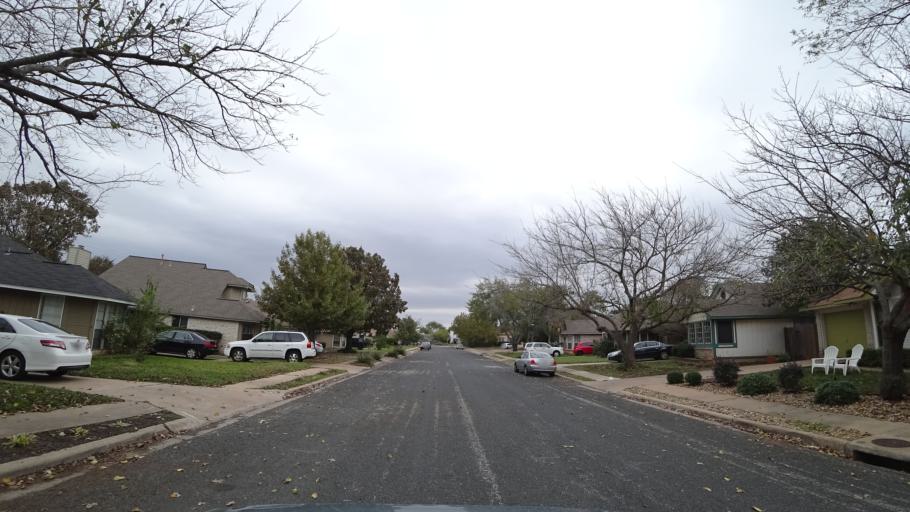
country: US
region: Texas
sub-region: Williamson County
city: Brushy Creek
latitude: 30.5092
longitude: -97.7406
